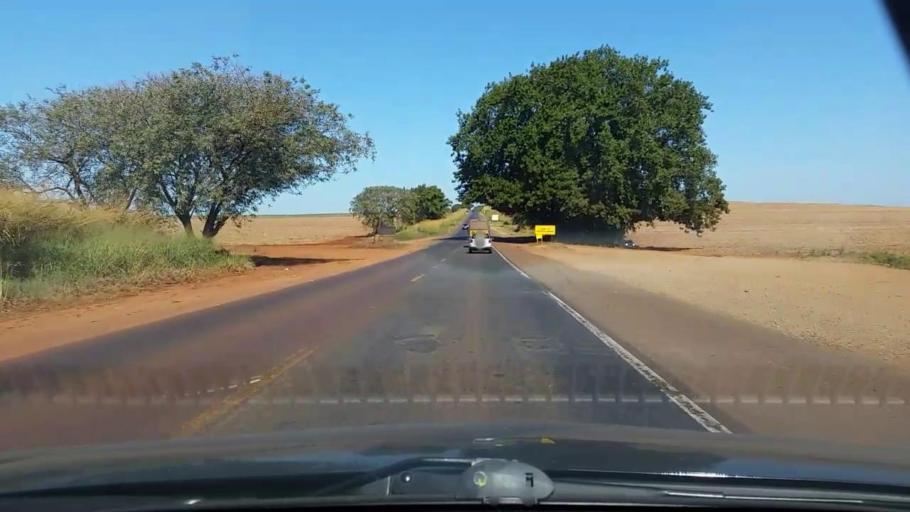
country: BR
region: Sao Paulo
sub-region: Igaracu Do Tiete
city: Igaracu do Tiete
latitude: -22.5720
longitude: -48.5638
